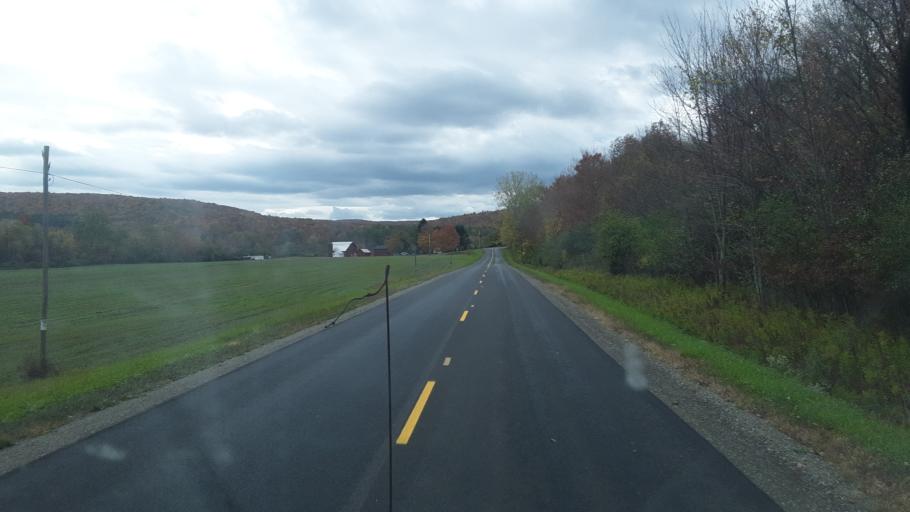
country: US
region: New York
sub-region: Allegany County
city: Alfred
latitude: 42.3668
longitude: -77.8158
